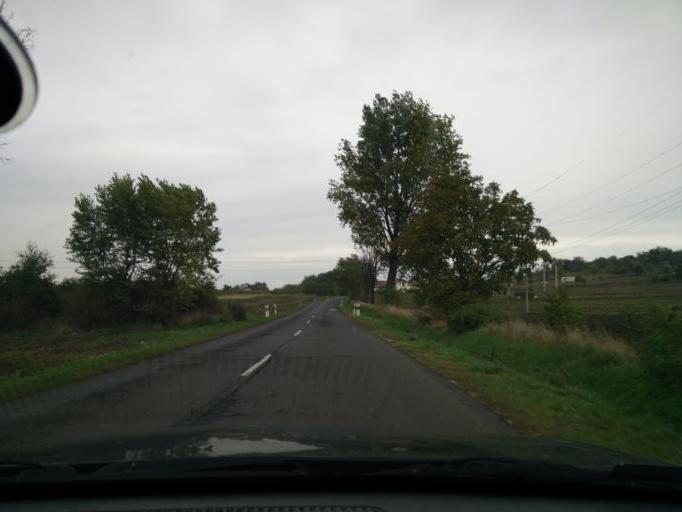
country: HU
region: Komarom-Esztergom
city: Tat
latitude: 47.7274
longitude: 18.6439
